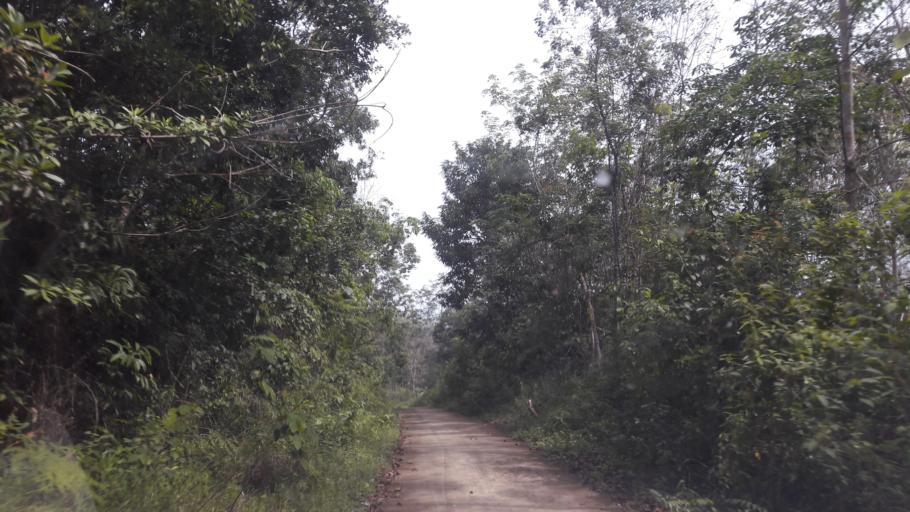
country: ID
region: South Sumatra
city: Gunungmenang
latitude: -3.1305
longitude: 103.8524
